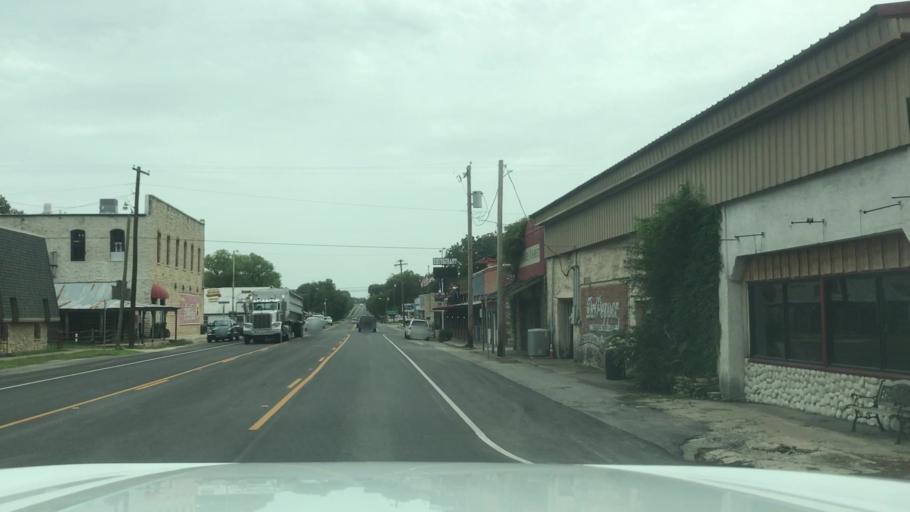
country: US
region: Texas
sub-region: Hamilton County
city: Hico
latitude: 31.9825
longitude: -98.0317
